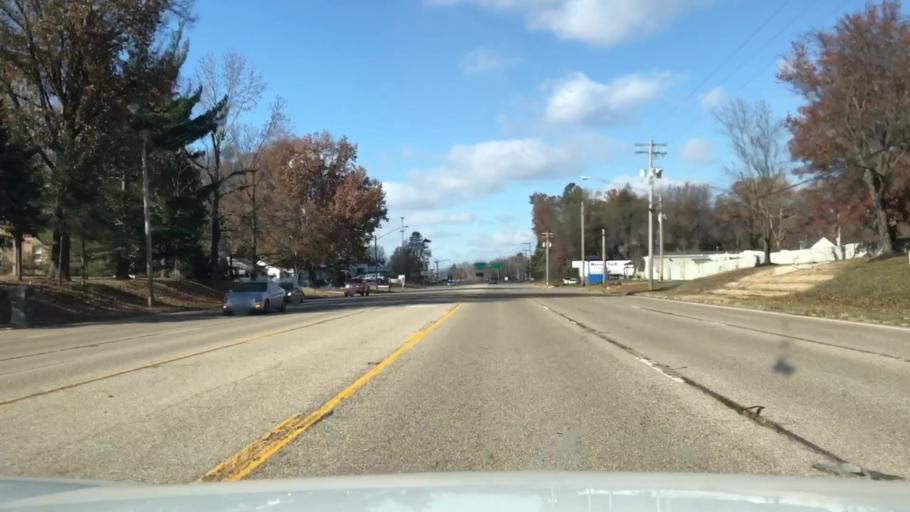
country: US
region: Illinois
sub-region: Saint Clair County
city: Swansea
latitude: 38.5383
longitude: -89.9933
